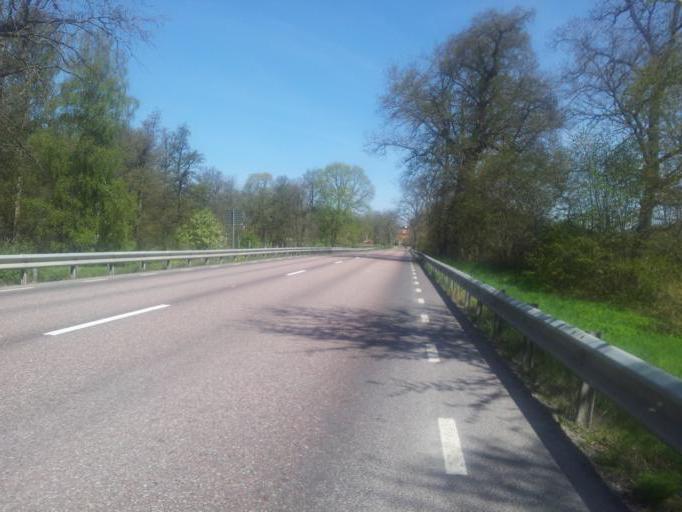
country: SE
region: Uppsala
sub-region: Knivsta Kommun
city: Knivsta
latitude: 59.8810
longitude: 17.9704
